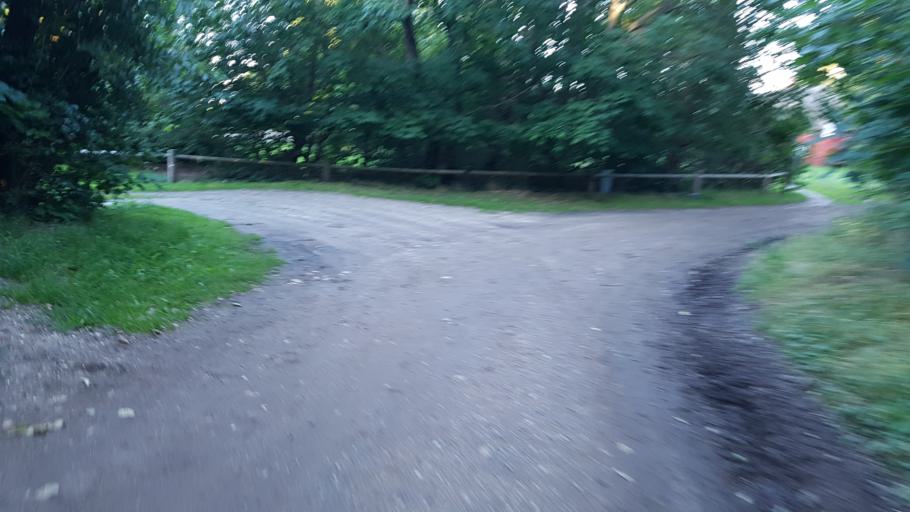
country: DE
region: Schleswig-Holstein
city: List
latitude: 55.1009
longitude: 8.5441
